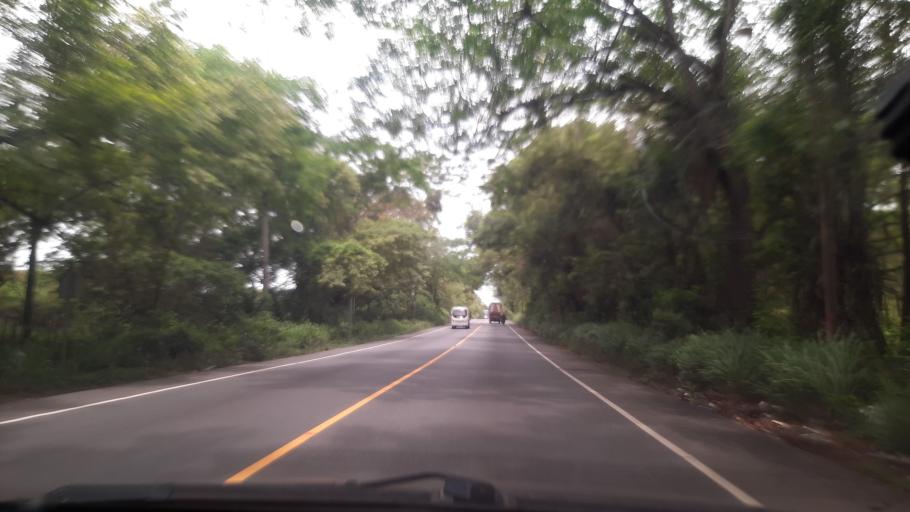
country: GT
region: Izabal
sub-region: Municipio de Los Amates
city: Los Amates
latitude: 15.2213
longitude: -89.2193
